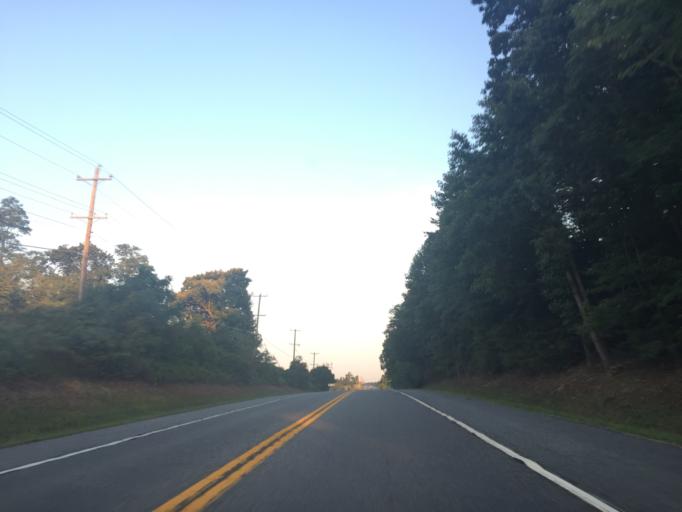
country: US
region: Pennsylvania
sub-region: York County
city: Susquehanna Trails
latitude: 39.6963
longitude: -76.3187
